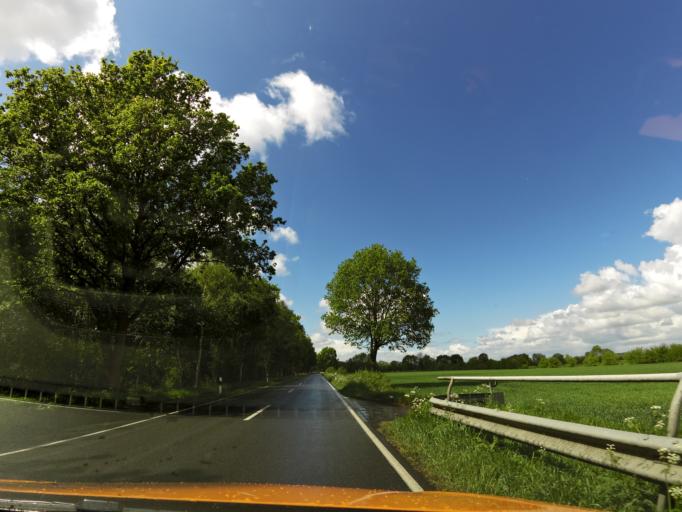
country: DE
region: Lower Saxony
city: Oldenburg
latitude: 53.1290
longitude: 8.2982
